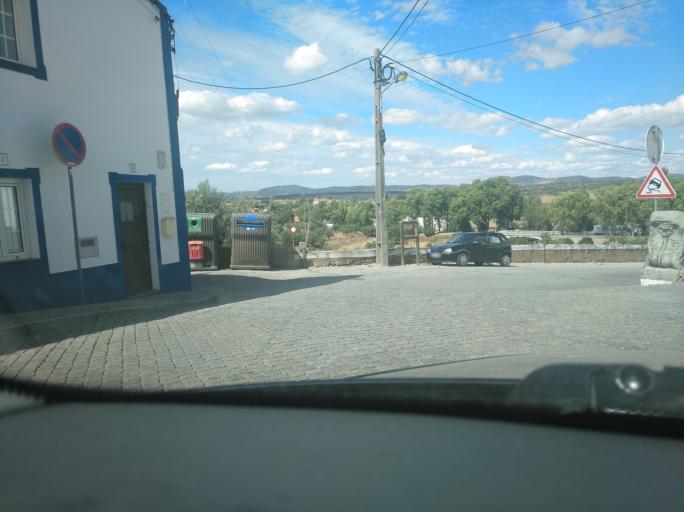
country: PT
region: Portalegre
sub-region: Arronches
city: Arronches
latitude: 39.1240
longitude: -7.2827
